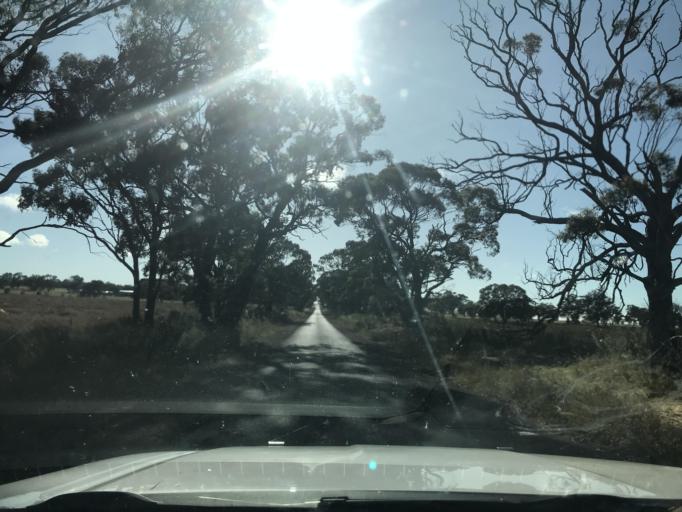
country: AU
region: Victoria
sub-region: Horsham
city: Horsham
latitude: -36.6990
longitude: 141.6139
